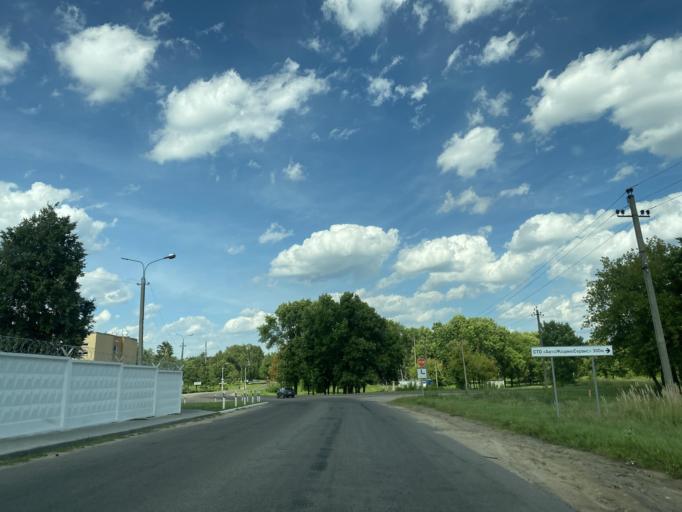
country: BY
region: Minsk
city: Horad Zhodzina
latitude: 54.0948
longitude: 28.3541
